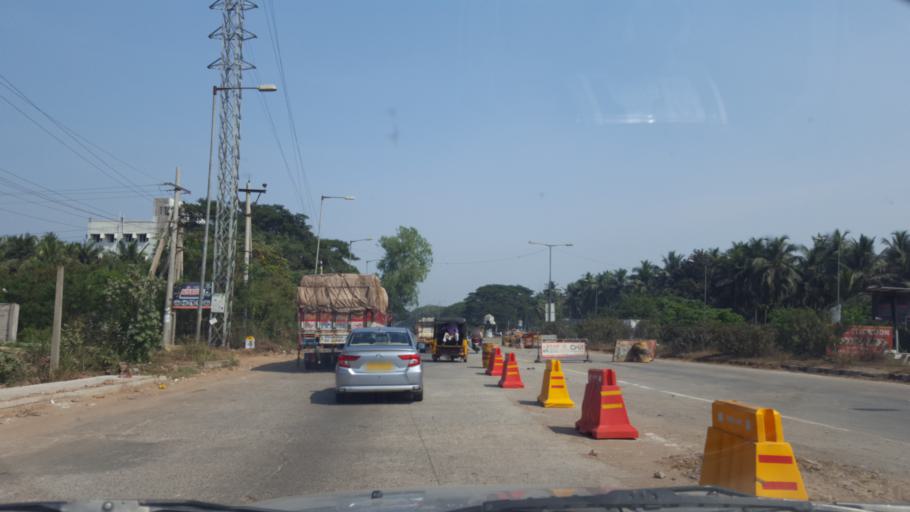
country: IN
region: Andhra Pradesh
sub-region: Vishakhapatnam
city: Anakapalle
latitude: 17.6751
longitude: 83.0050
